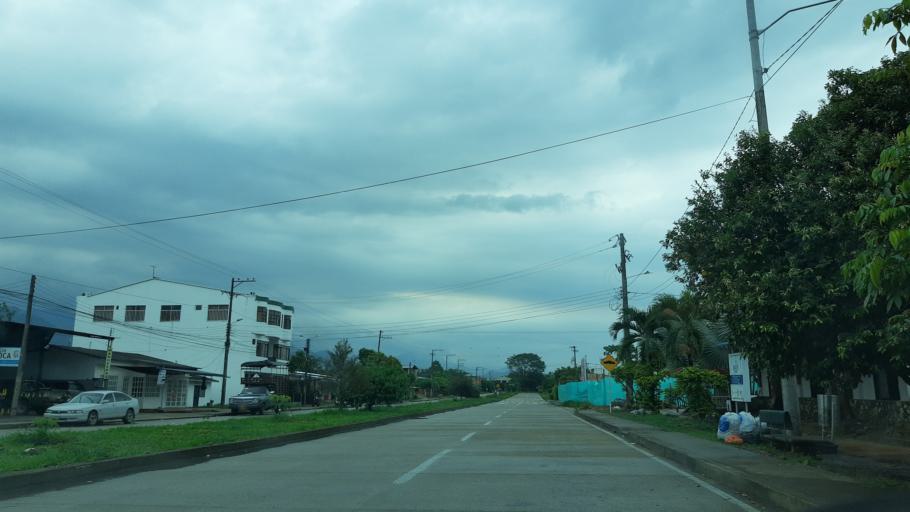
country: CO
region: Casanare
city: Monterrey
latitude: 4.8842
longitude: -72.8936
